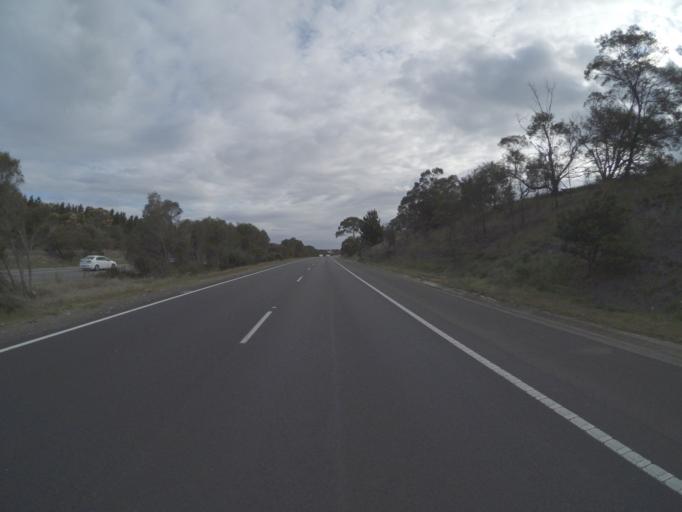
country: AU
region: New South Wales
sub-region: Wingecarribee
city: Bundanoon
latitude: -34.6002
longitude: 150.2363
